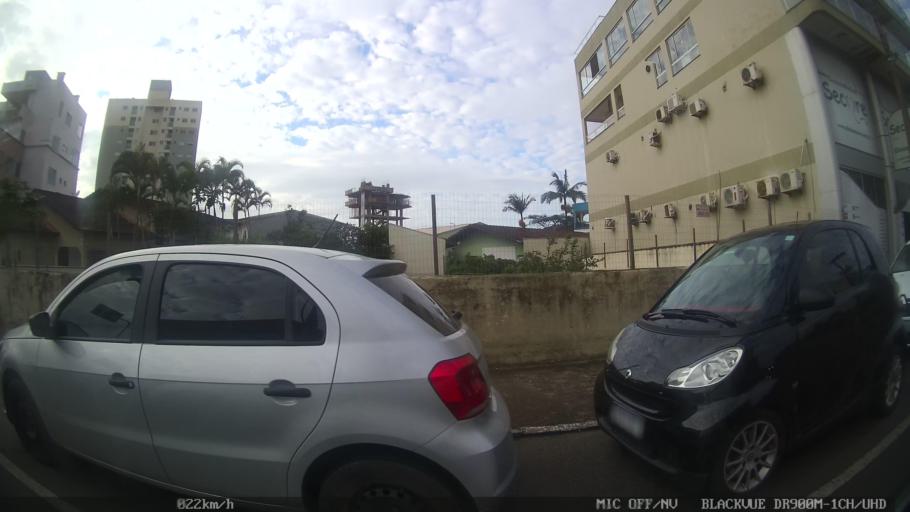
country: BR
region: Santa Catarina
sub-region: Barra Velha
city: Barra Velha
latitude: -26.6441
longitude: -48.6856
